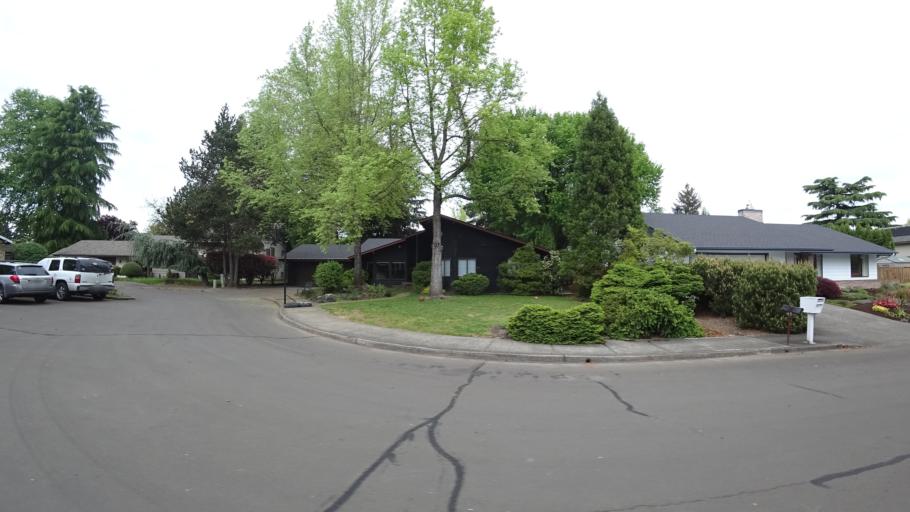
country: US
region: Oregon
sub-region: Washington County
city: Hillsboro
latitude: 45.4927
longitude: -122.9541
